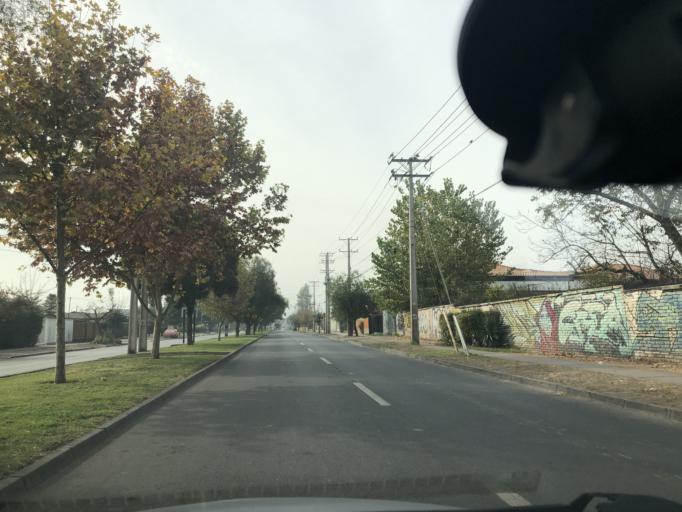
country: CL
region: Santiago Metropolitan
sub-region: Provincia de Cordillera
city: Puente Alto
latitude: -33.5803
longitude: -70.5741
